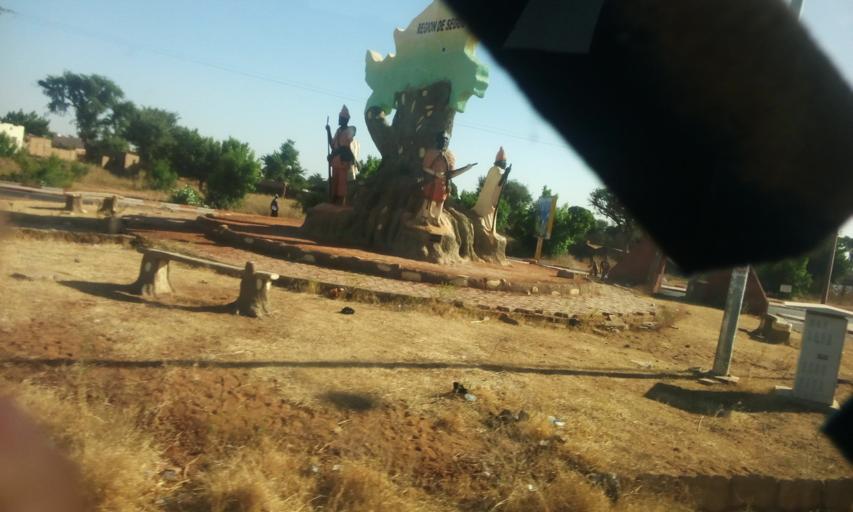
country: ML
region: Segou
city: Segou
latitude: 13.4147
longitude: -6.3232
